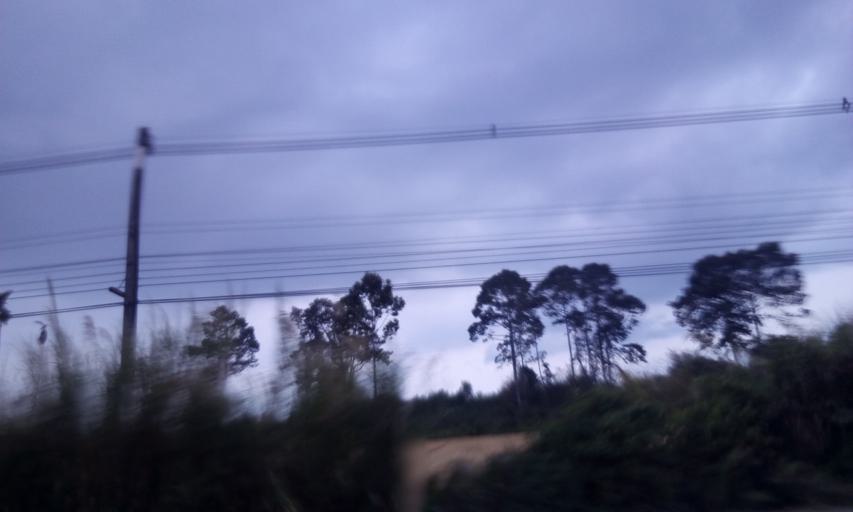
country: TH
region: Chanthaburi
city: Khlung
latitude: 12.4551
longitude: 102.2760
